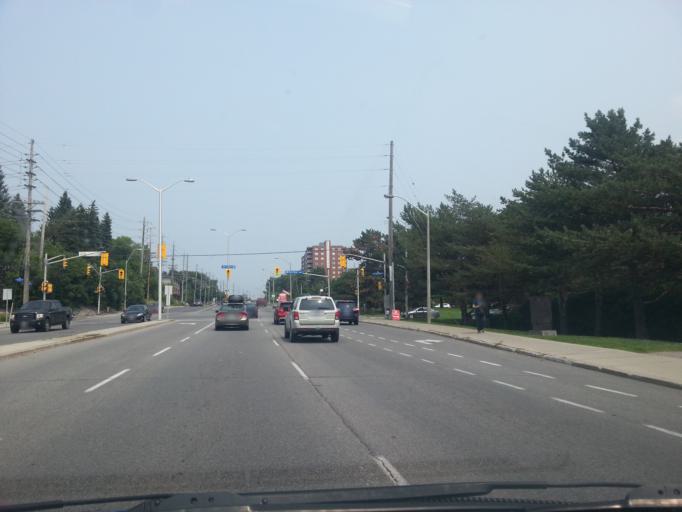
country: CA
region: Ontario
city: Ottawa
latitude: 45.4443
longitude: -75.6369
